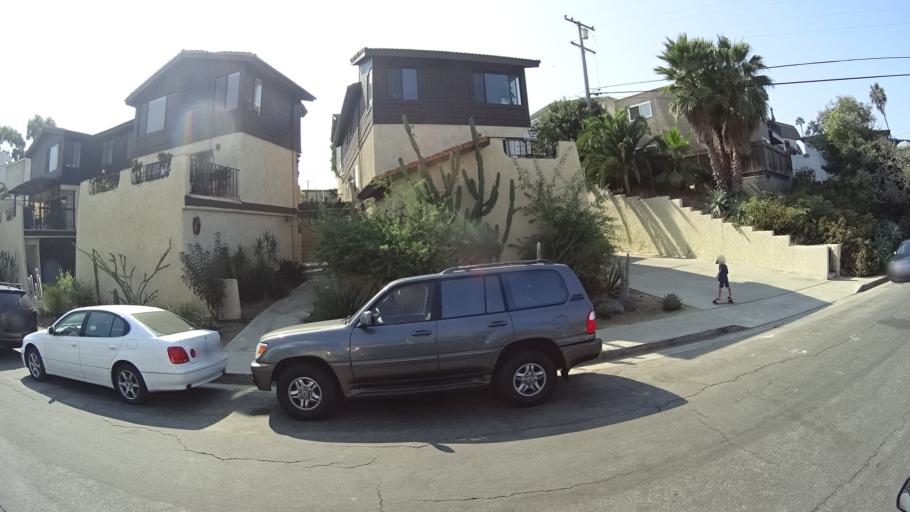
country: US
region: California
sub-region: Orange County
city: San Clemente
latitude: 33.4275
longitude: -117.6264
